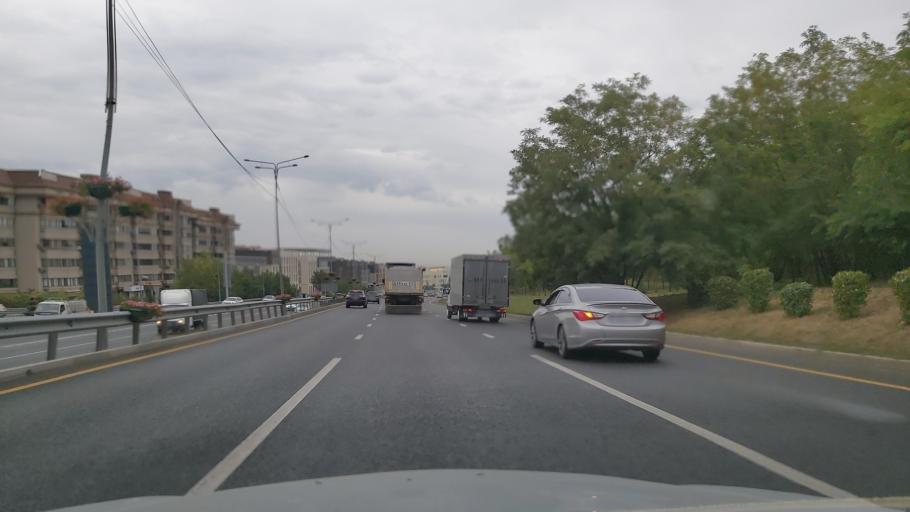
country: KZ
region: Almaty Qalasy
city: Almaty
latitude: 43.2572
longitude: 76.9831
